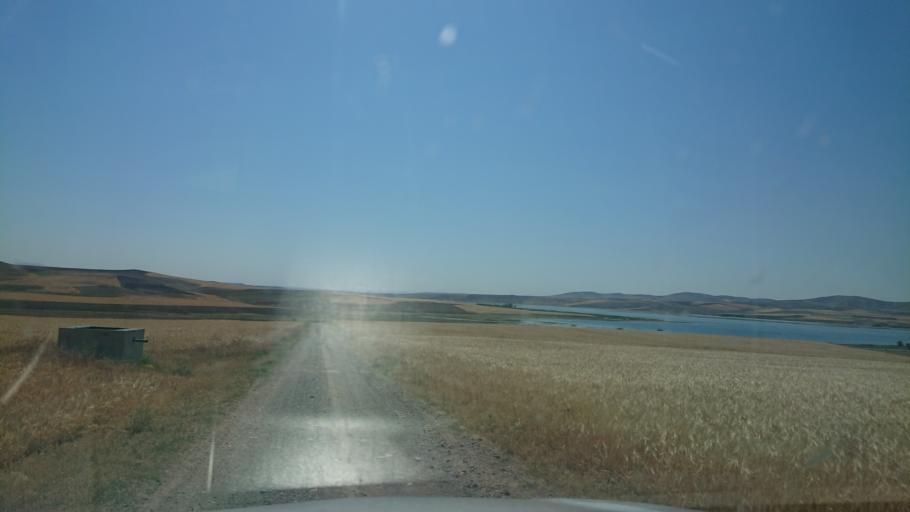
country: TR
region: Aksaray
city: Sariyahsi
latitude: 39.0556
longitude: 33.8940
